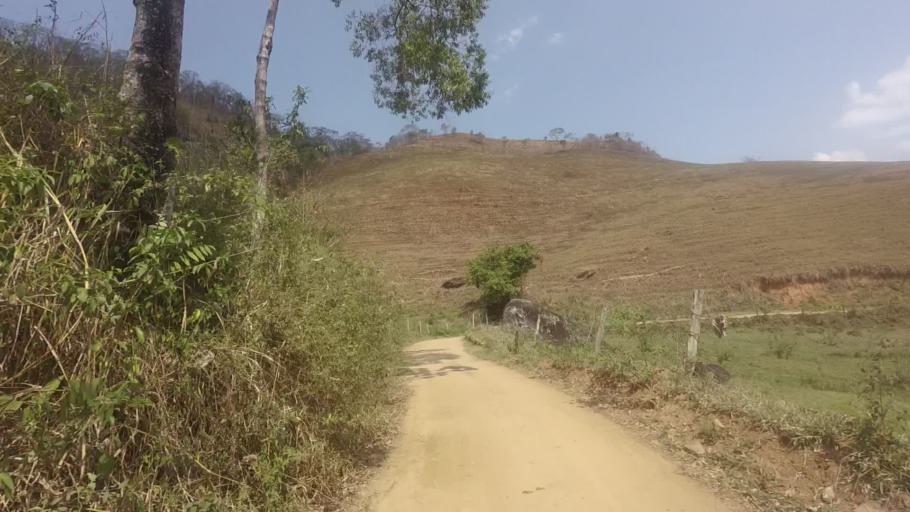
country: BR
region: Espirito Santo
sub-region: Sao Jose Do Calcado
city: Sao Jose do Calcado
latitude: -21.0101
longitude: -41.5100
